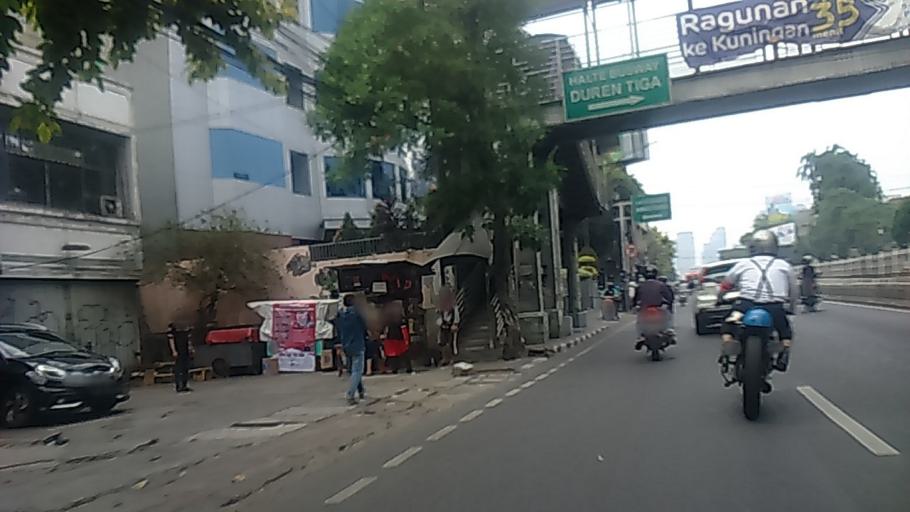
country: ID
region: Jakarta Raya
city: Jakarta
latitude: -6.2528
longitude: 106.8271
